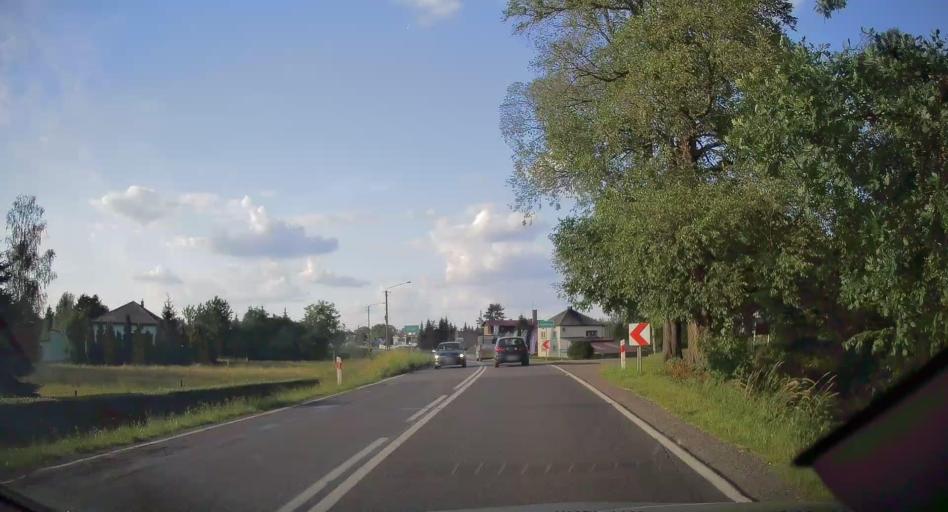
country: PL
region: Lesser Poland Voivodeship
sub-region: Powiat oswiecimski
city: Oswiecim
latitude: 50.0165
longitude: 19.2131
